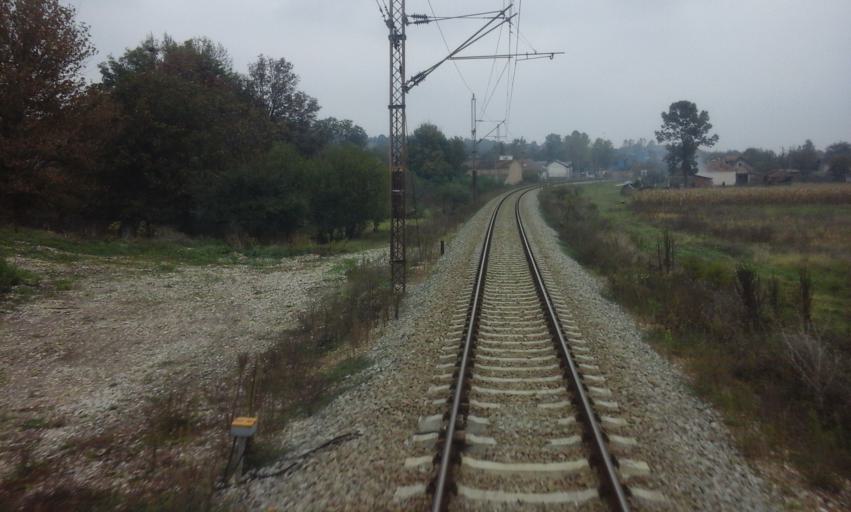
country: RS
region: Central Serbia
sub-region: Belgrade
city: Mladenovac
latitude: 44.4782
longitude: 20.6622
